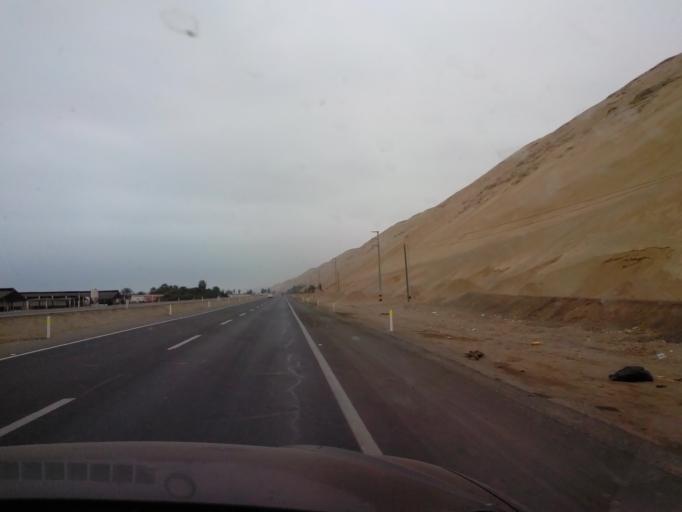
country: PE
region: Ica
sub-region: Provincia de Chincha
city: San Pedro
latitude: -13.3563
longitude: -76.2196
